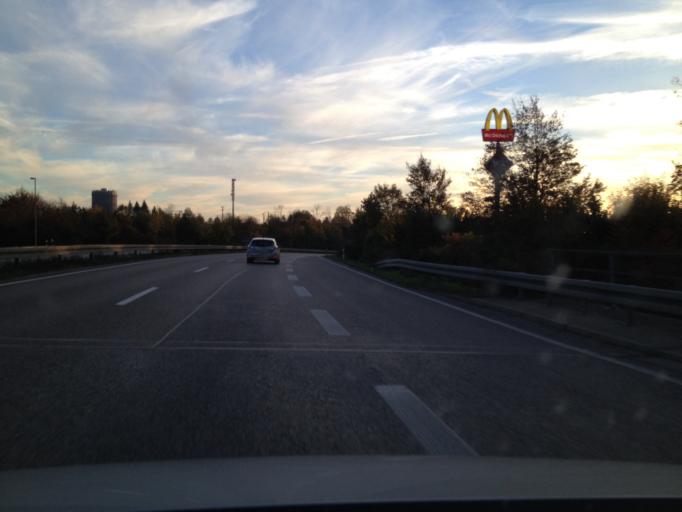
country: DE
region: Bavaria
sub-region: Swabia
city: Gersthofen
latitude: 48.3991
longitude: 10.8697
